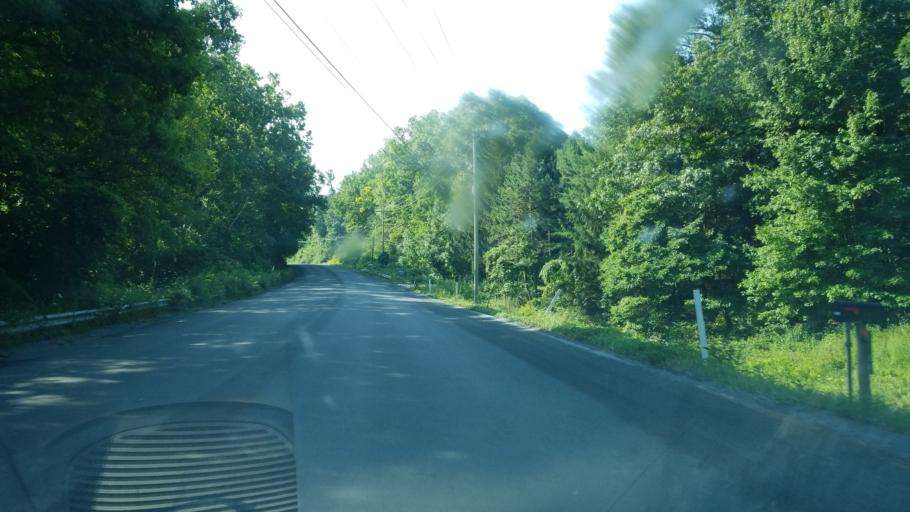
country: US
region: Michigan
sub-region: Kent County
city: Comstock Park
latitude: 43.1104
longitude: -85.6474
